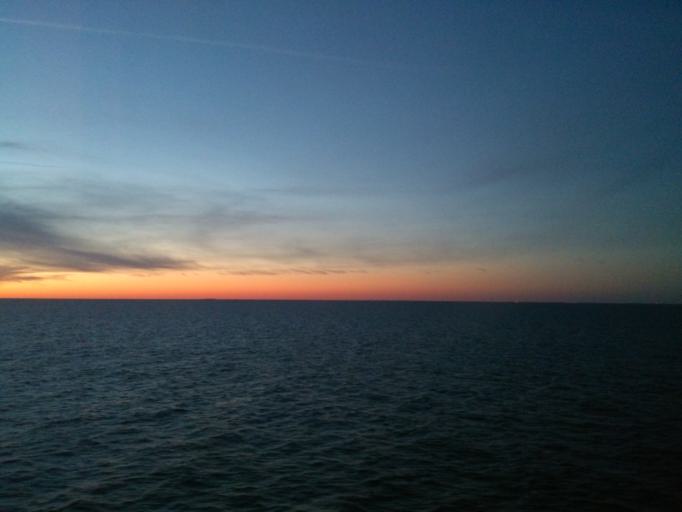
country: FI
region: Uusimaa
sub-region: Raaseporin
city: Hanko
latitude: 59.5888
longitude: 22.7295
